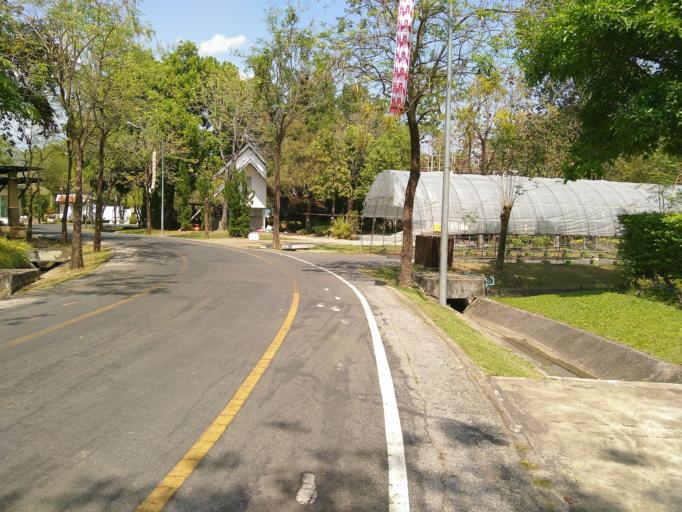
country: TH
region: Chiang Mai
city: Hang Dong
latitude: 18.7496
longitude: 98.9260
